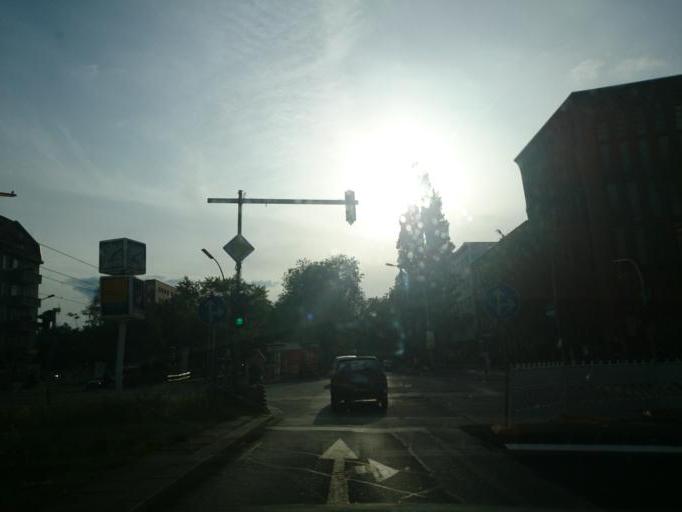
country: DE
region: Berlin
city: Gesundbrunnen
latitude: 52.5560
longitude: 13.3849
